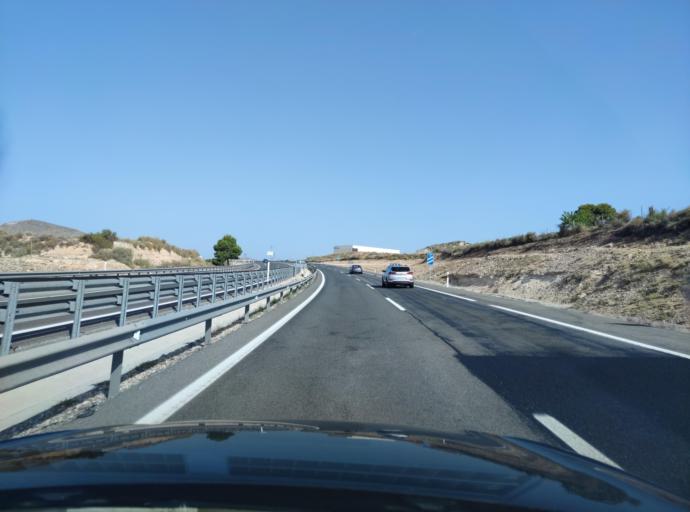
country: ES
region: Valencia
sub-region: Provincia de Alicante
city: Novelda
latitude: 38.4048
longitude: -0.7660
